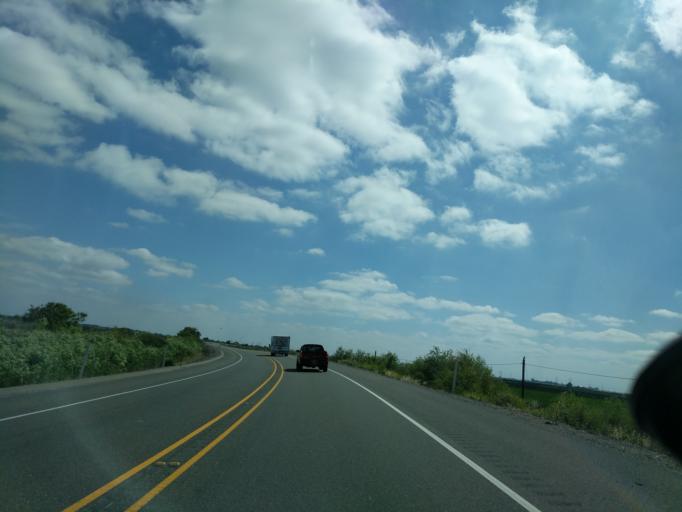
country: US
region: California
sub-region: Contra Costa County
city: Discovery Bay
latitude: 37.8985
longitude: -121.4737
